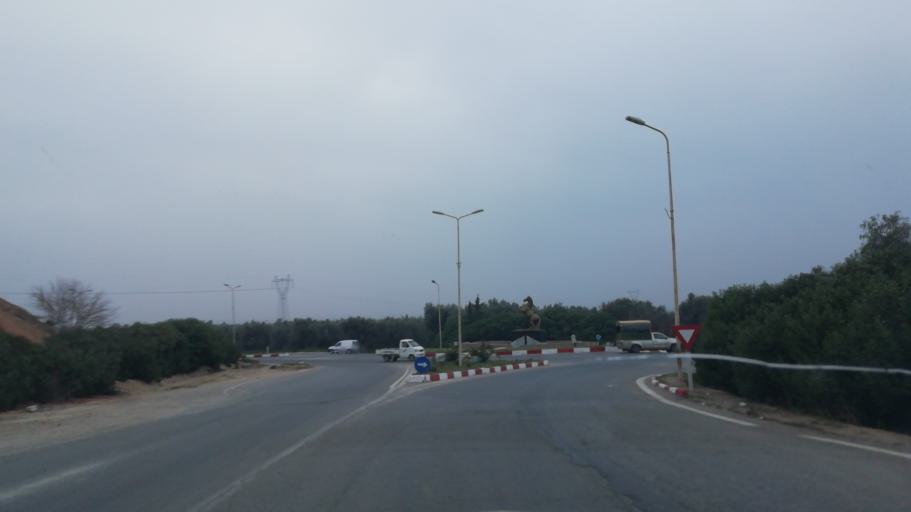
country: DZ
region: Mascara
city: Mascara
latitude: 35.3819
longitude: 0.1619
